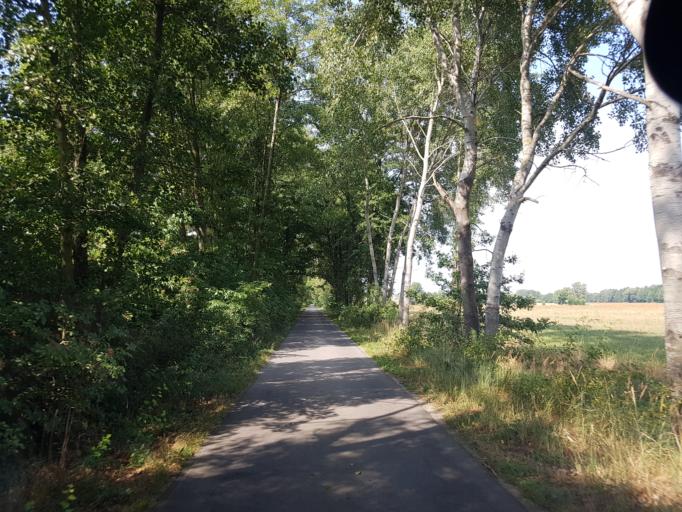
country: DE
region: Brandenburg
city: Finsterwalde
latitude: 51.6624
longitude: 13.7497
